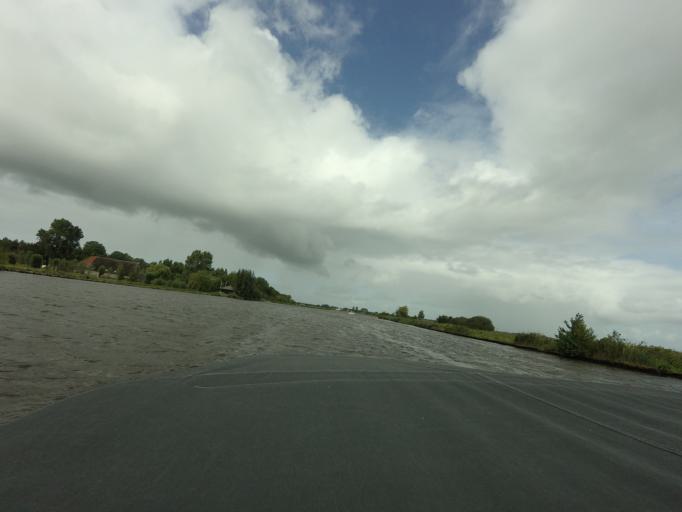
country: NL
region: Friesland
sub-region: Gemeente Boarnsterhim
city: Warten
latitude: 53.1380
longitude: 5.9154
